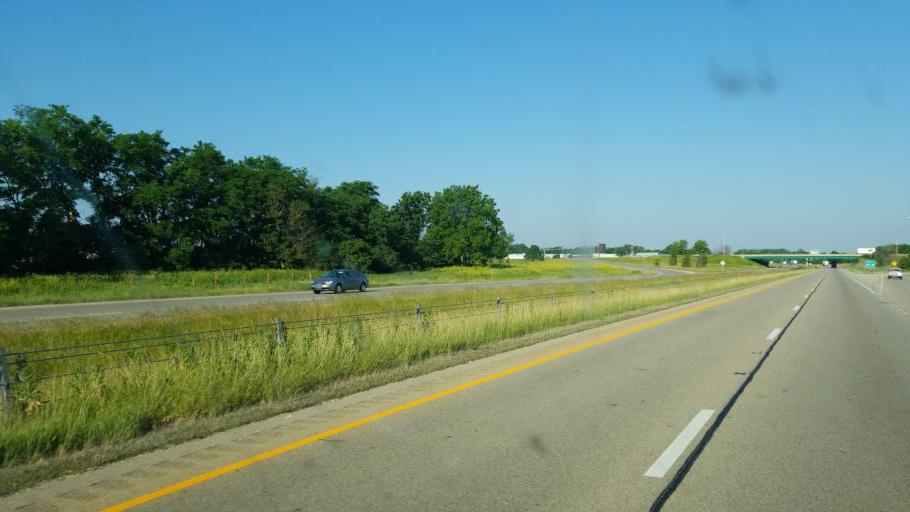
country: US
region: Illinois
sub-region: LaSalle County
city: Ottawa
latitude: 41.3763
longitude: -88.8309
